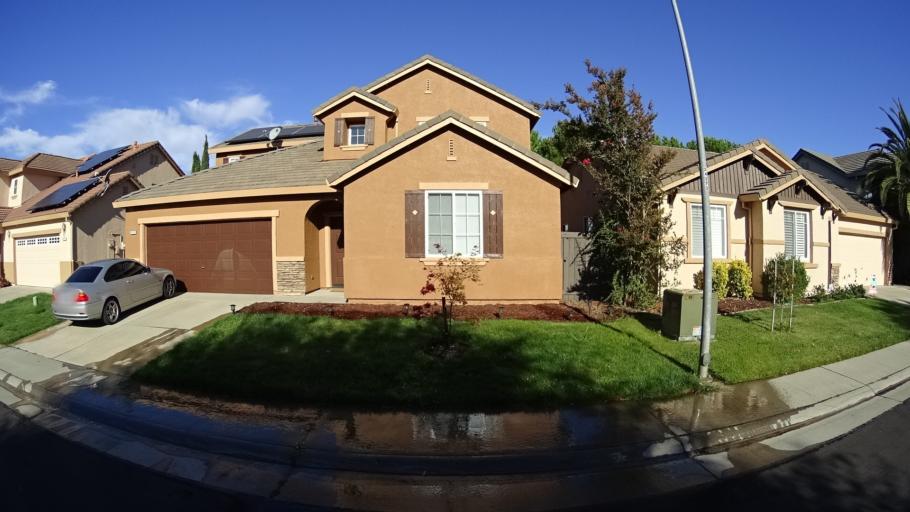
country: US
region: California
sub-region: Sacramento County
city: Laguna
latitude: 38.4057
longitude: -121.4750
